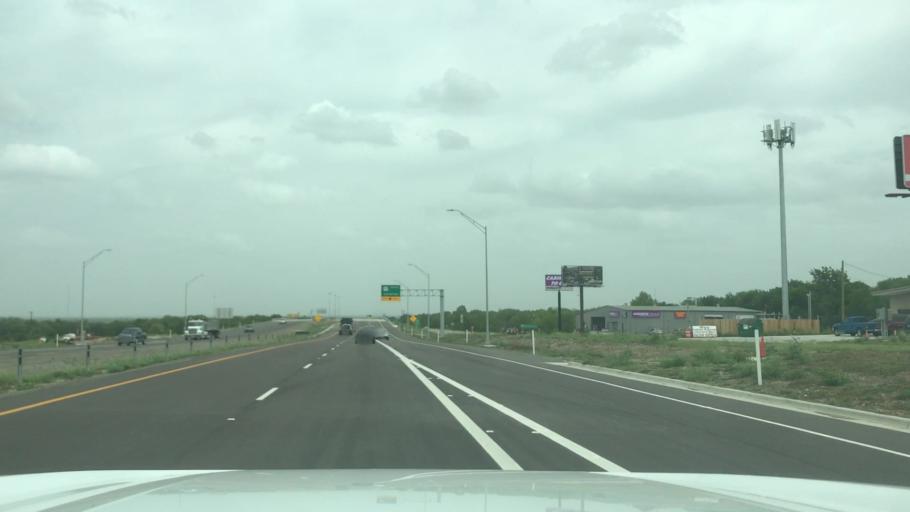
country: US
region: Texas
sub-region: McLennan County
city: Beverly
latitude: 31.4930
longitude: -97.1368
